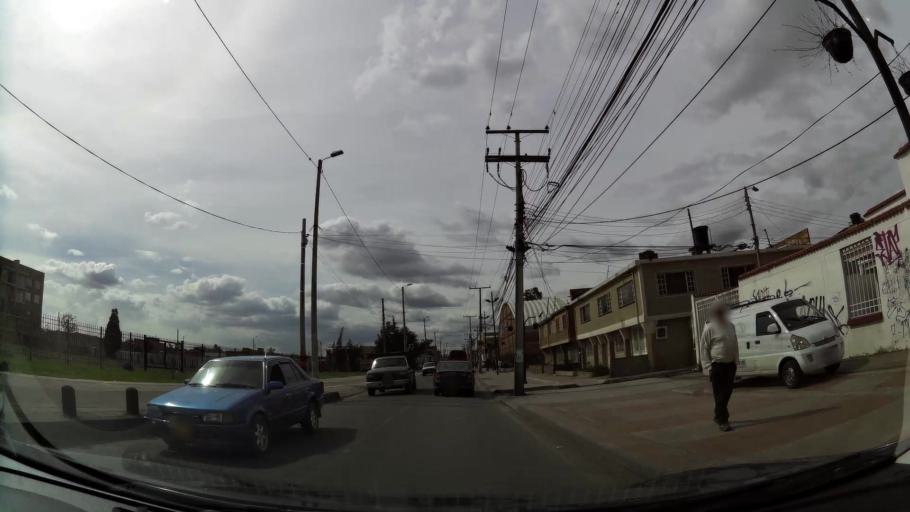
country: CO
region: Cundinamarca
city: Funza
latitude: 4.7061
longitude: -74.2048
